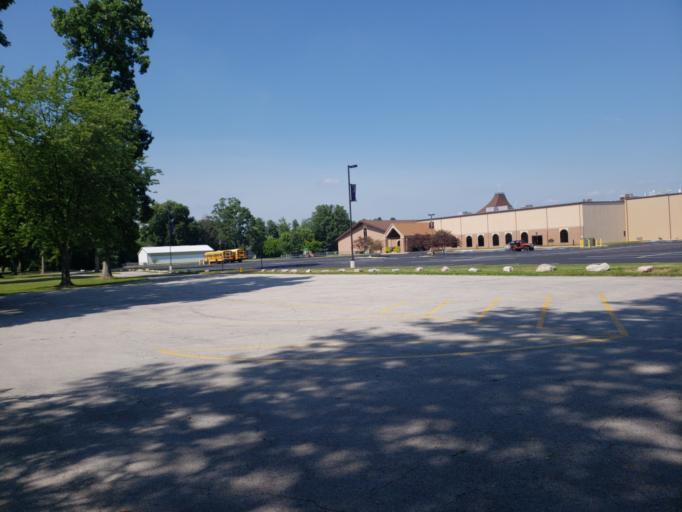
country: US
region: Ohio
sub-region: Sandusky County
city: Fremont
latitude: 41.3333
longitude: -83.0937
